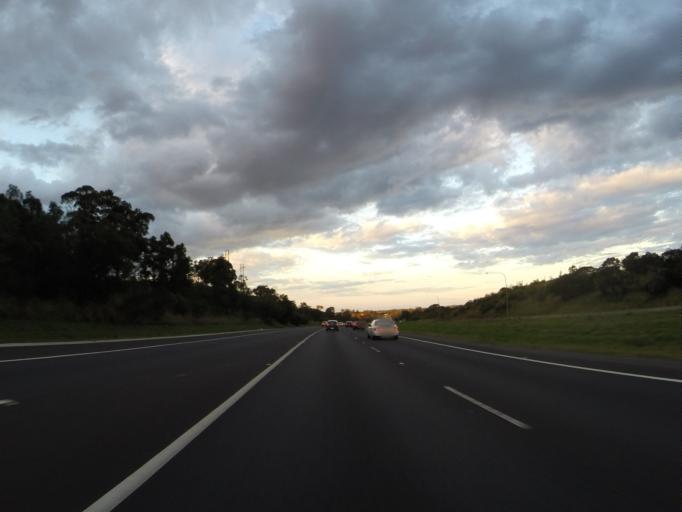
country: AU
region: New South Wales
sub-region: Campbelltown Municipality
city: Campbelltown
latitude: -34.0588
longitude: 150.7906
